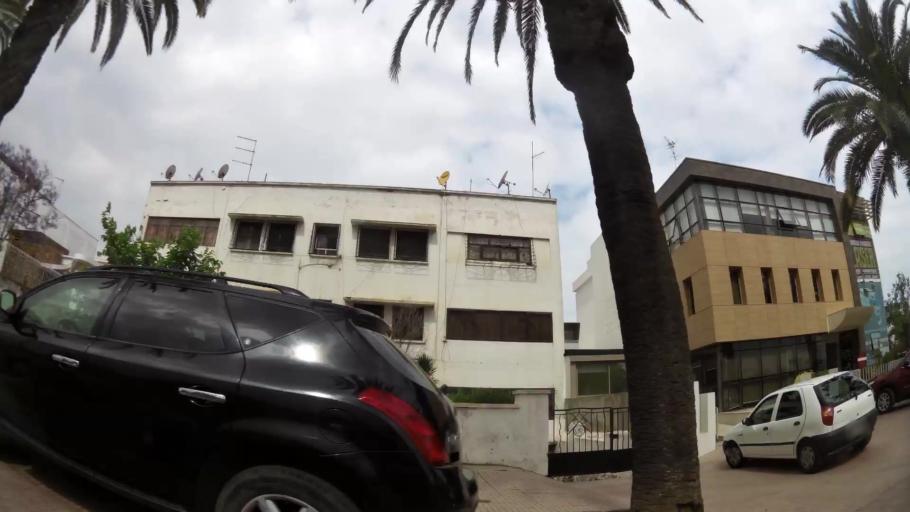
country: MA
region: Rabat-Sale-Zemmour-Zaer
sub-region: Rabat
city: Rabat
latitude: 34.0071
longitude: -6.8440
